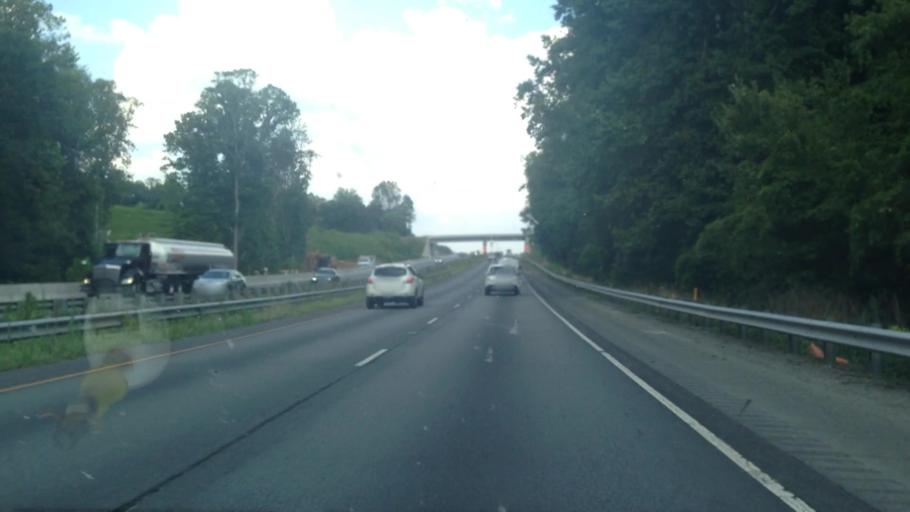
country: US
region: North Carolina
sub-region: Forsyth County
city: Walkertown
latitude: 36.1137
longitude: -80.1479
